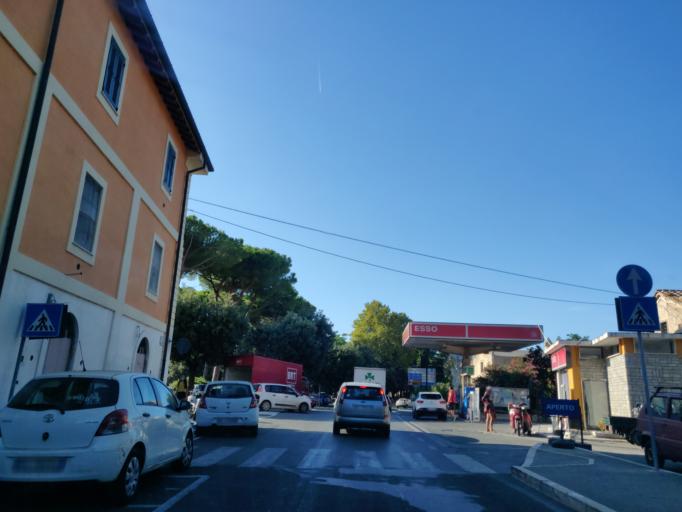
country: IT
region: Tuscany
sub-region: Provincia di Grosseto
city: Orbetello
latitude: 42.4392
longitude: 11.2140
